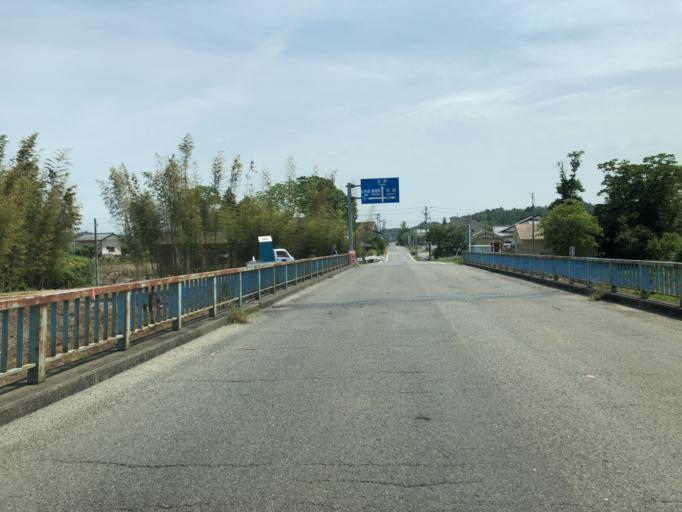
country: JP
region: Fukushima
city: Namie
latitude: 37.4859
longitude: 140.9980
